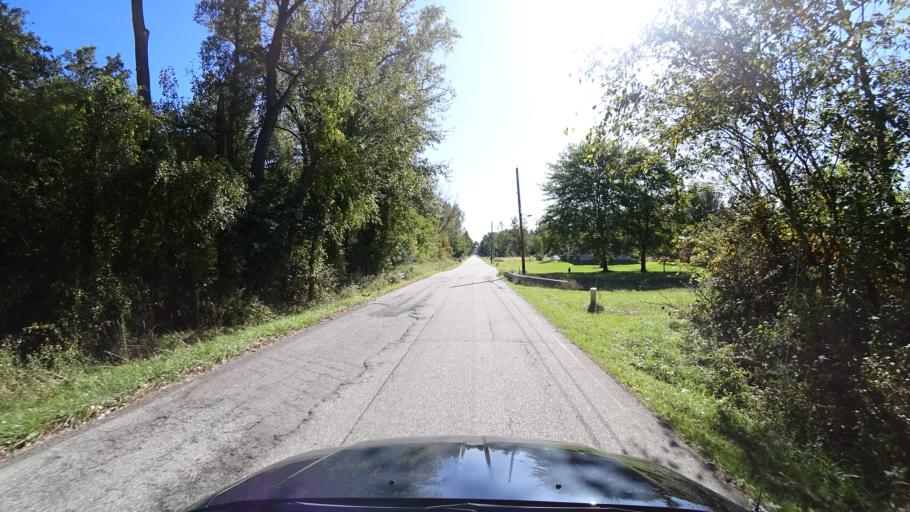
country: US
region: Indiana
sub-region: LaPorte County
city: Long Beach
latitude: 41.7419
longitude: -86.8161
